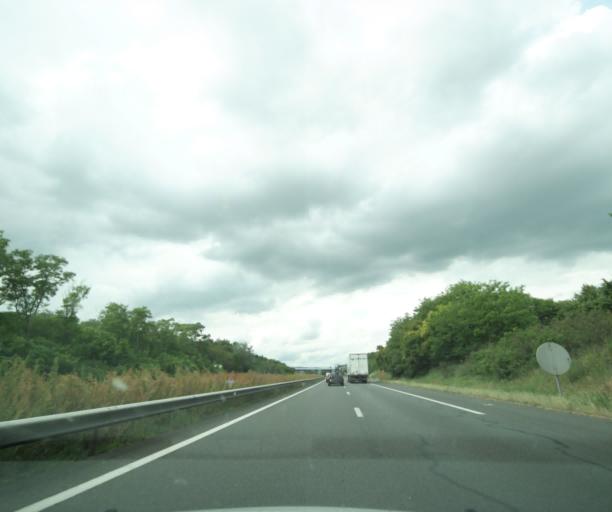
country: FR
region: Auvergne
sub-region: Departement du Puy-de-Dome
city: Saint-Bonnet-pres-Riom
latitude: 45.9231
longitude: 3.1446
